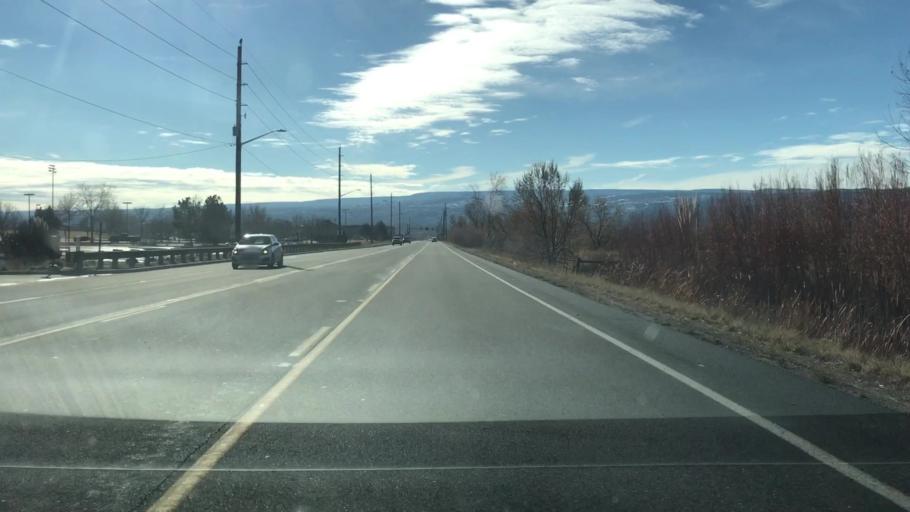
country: US
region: Colorado
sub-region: Mesa County
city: Redlands
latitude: 39.1105
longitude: -108.6082
